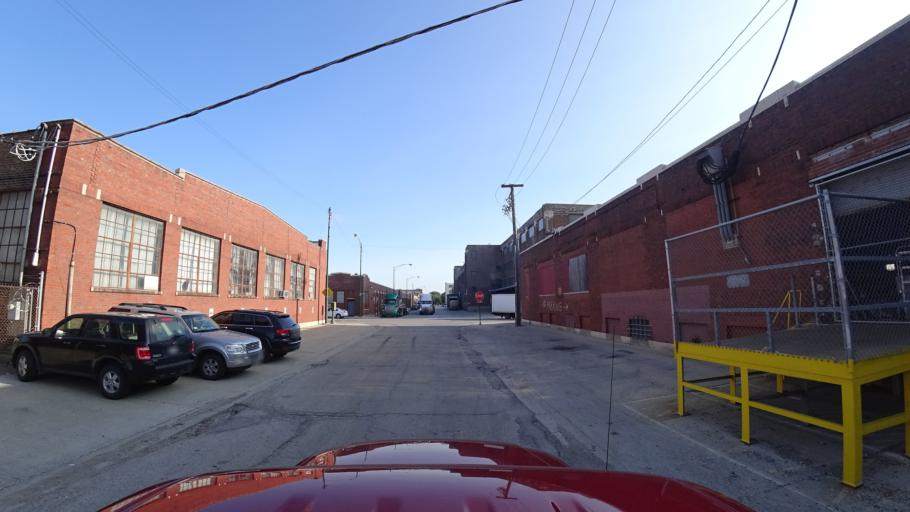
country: US
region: Illinois
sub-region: Cook County
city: Cicero
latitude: 41.8053
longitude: -87.7075
